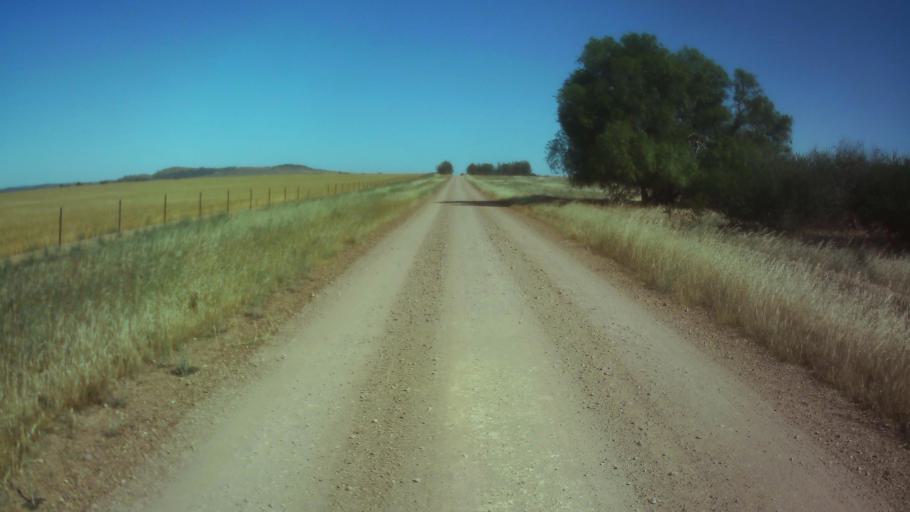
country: AU
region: New South Wales
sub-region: Weddin
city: Grenfell
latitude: -33.9871
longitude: 148.3351
